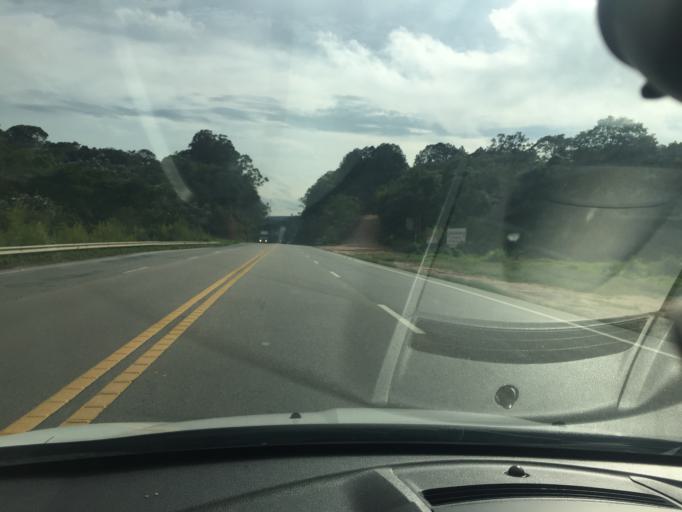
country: BR
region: Sao Paulo
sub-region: Campo Limpo Paulista
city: Campo Limpo Paulista
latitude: -23.1691
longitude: -46.7647
